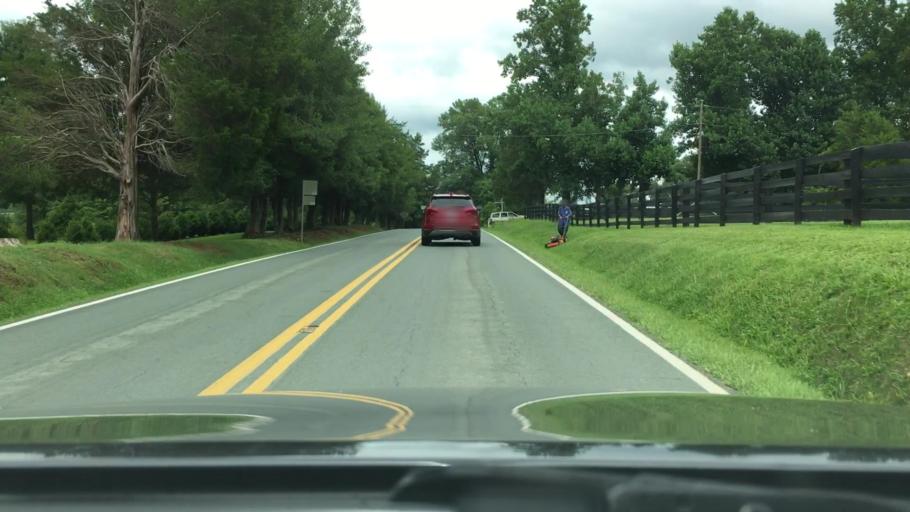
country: US
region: Virginia
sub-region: Fluvanna County
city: Lake Monticello
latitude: 38.0255
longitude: -78.3548
